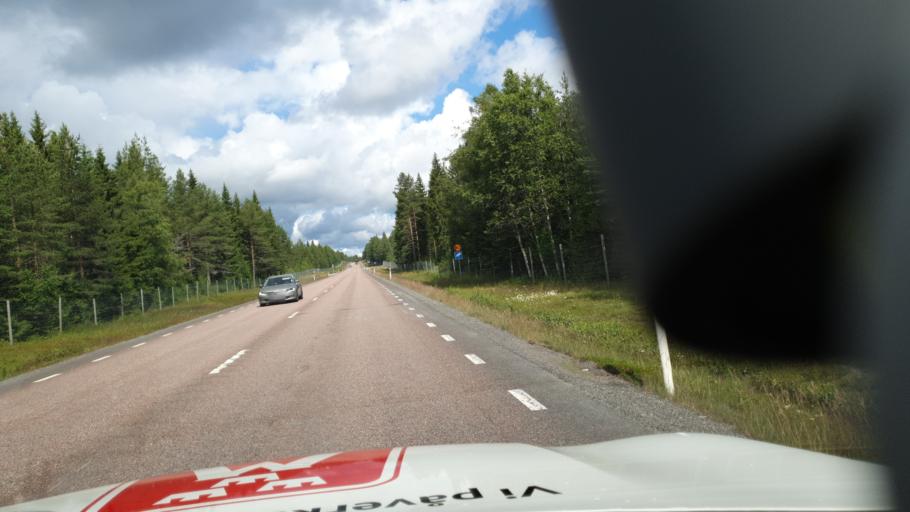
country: SE
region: Vaesterbotten
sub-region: Skelleftea Kommun
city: Burea
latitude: 64.4228
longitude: 21.2857
